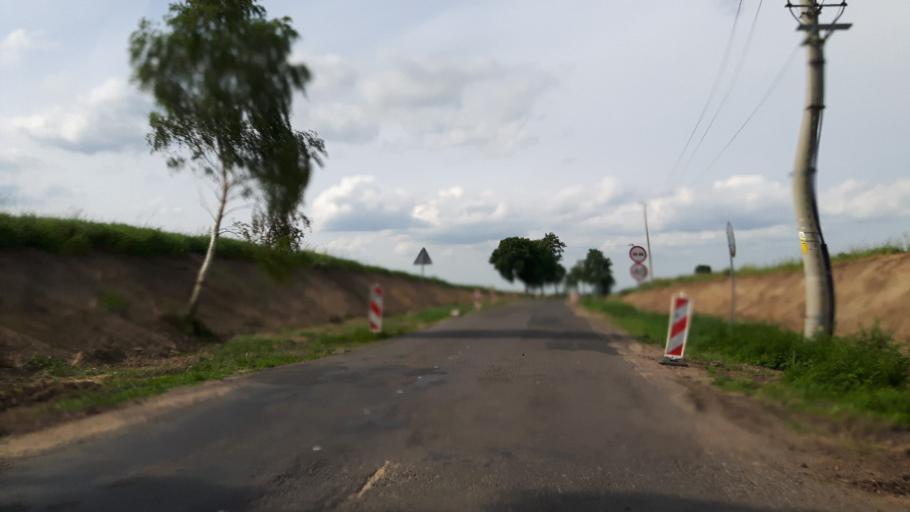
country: PL
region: West Pomeranian Voivodeship
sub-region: Powiat goleniowski
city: Nowogard
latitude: 53.6962
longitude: 15.1168
